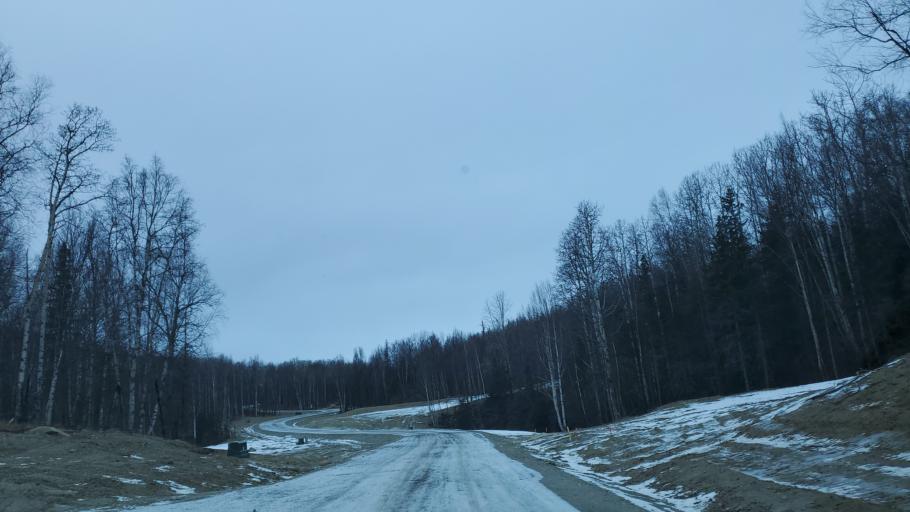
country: US
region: Alaska
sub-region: Matanuska-Susitna Borough
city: Gateway
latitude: 61.6550
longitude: -149.2306
